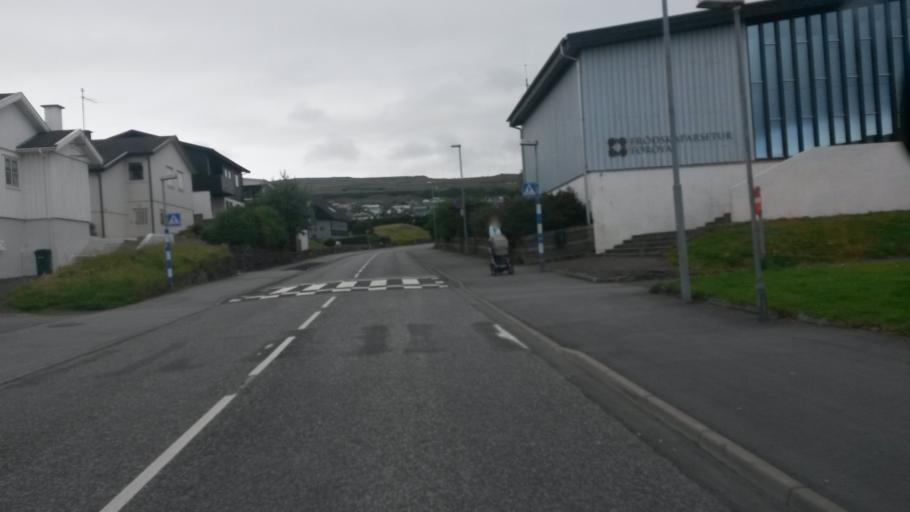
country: FO
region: Streymoy
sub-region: Torshavn
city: Torshavn
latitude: 62.0053
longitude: -6.7826
